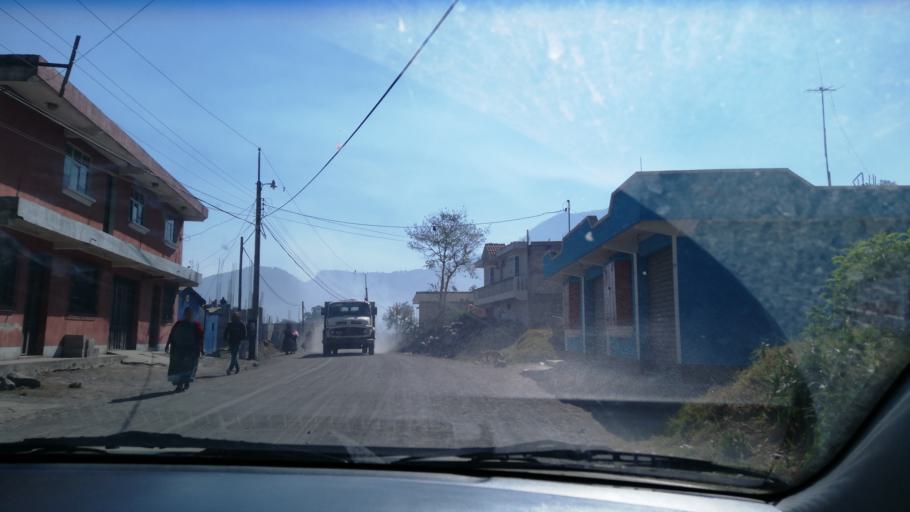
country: GT
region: Quetzaltenango
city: Quetzaltenango
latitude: 14.8054
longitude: -91.5523
